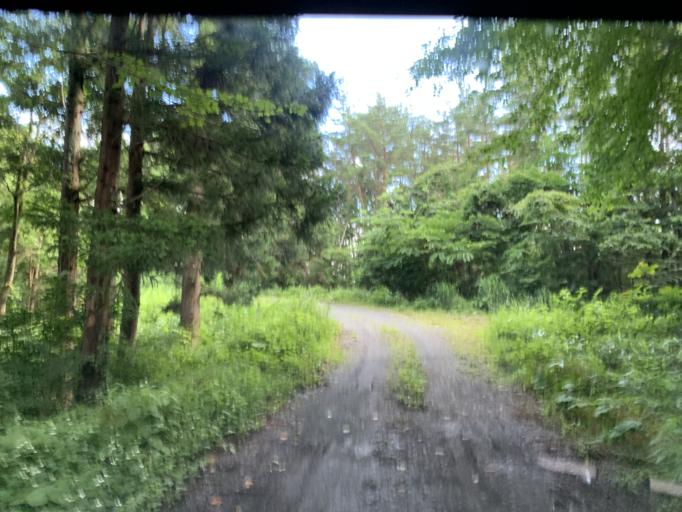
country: JP
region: Iwate
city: Ichinoseki
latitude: 38.9047
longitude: 140.9515
